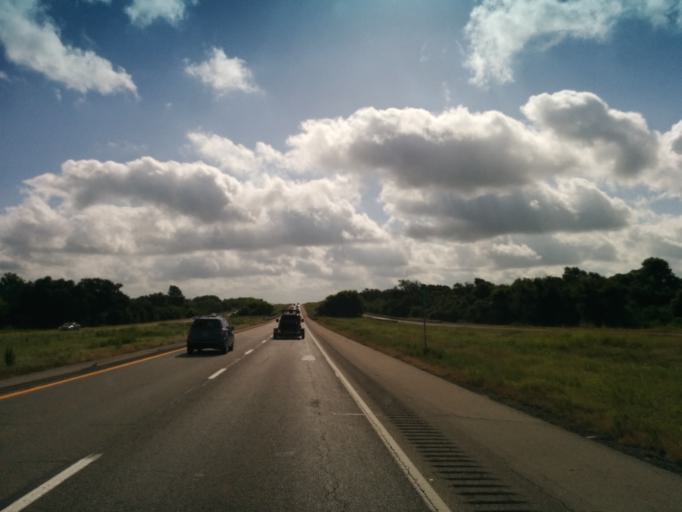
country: US
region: Texas
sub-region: Caldwell County
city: Luling
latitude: 29.6322
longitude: -97.7440
